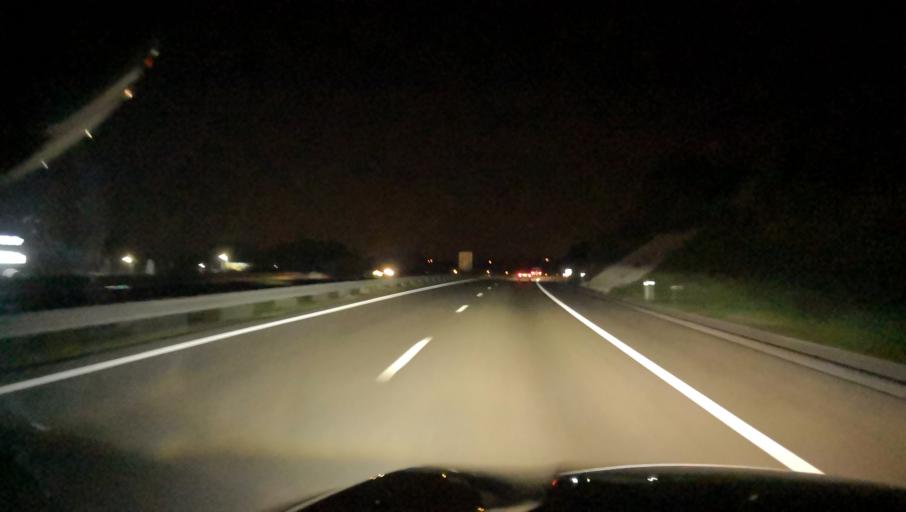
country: PT
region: Aveiro
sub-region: Mealhada
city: Mealhada
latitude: 40.3641
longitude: -8.4927
